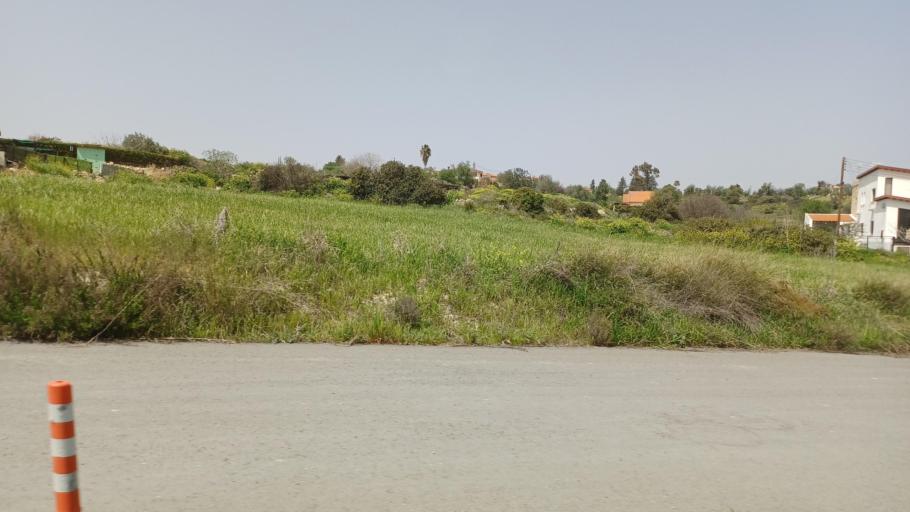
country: CY
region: Limassol
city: Pachna
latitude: 34.7376
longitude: 32.7388
